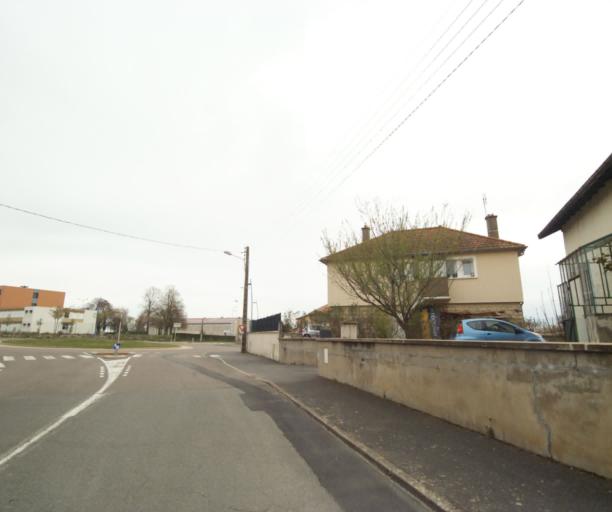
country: FR
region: Bourgogne
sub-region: Departement de Saone-et-Loire
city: Charnay-les-Macon
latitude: 46.2972
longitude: 4.8048
